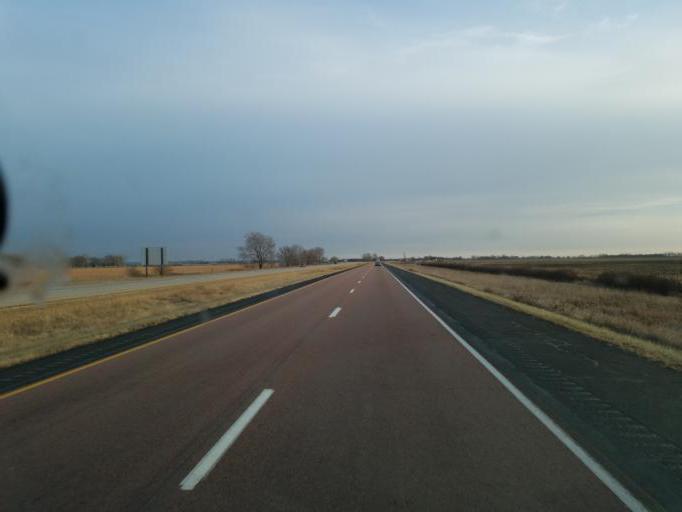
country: US
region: Iowa
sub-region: Monona County
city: Onawa
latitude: 42.0140
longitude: -96.1225
